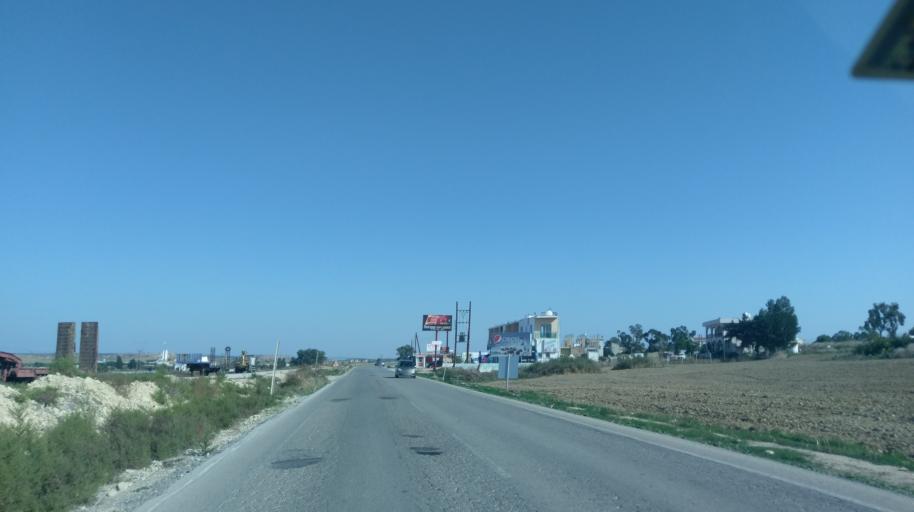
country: CY
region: Ammochostos
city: Trikomo
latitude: 35.3666
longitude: 34.0228
